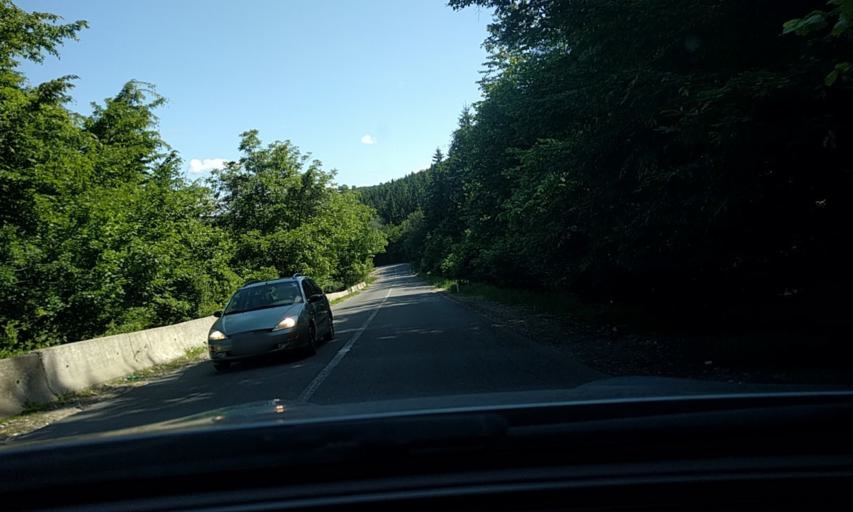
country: RO
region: Bistrita-Nasaud
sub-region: Comuna Dumitra
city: Dumitra
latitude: 47.1906
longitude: 24.4803
